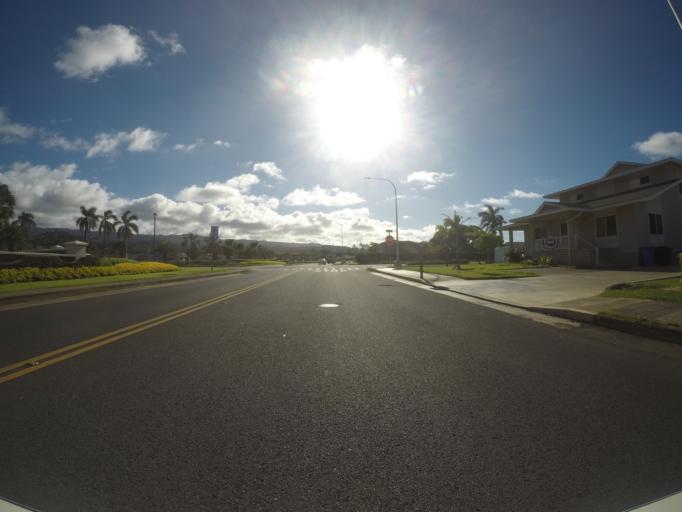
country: US
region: Hawaii
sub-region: Honolulu County
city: La'ie
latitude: 21.6443
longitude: -157.9245
